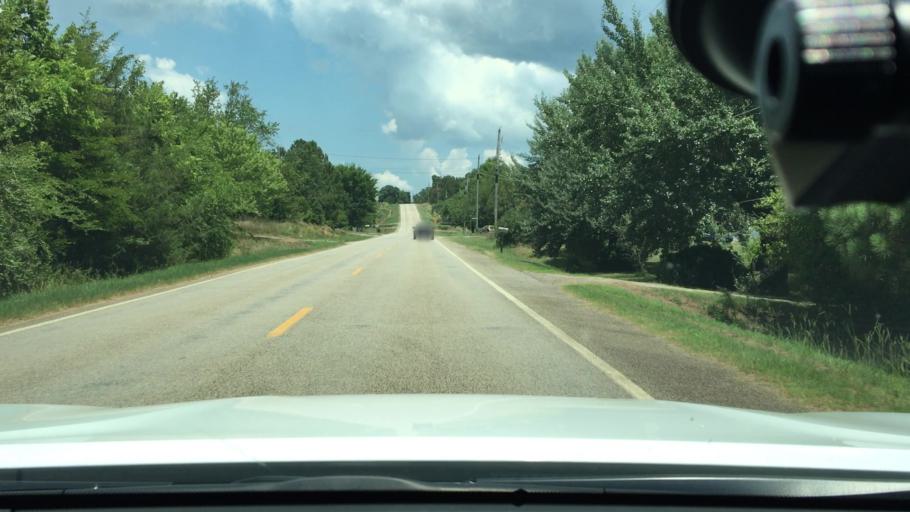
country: US
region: Arkansas
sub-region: Logan County
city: Booneville
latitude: 35.1524
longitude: -93.8770
